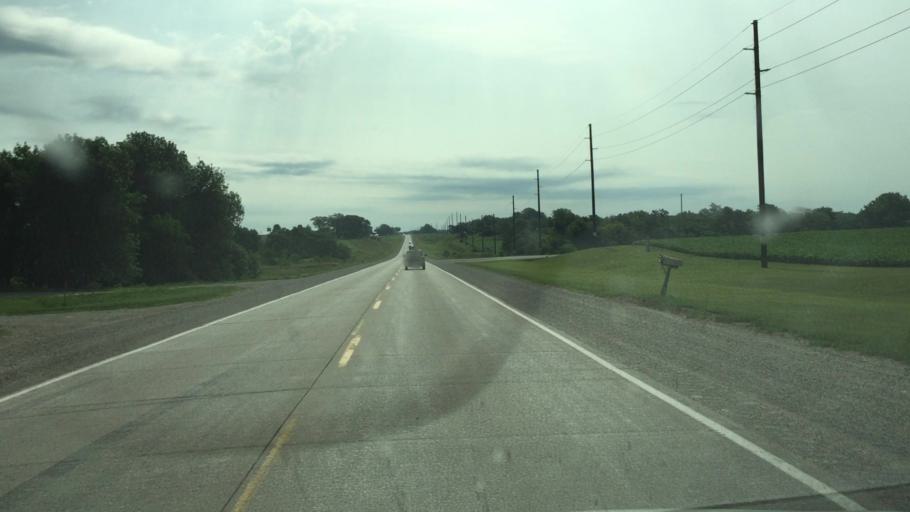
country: US
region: Illinois
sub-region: Hancock County
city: Nauvoo
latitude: 40.6390
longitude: -91.5484
